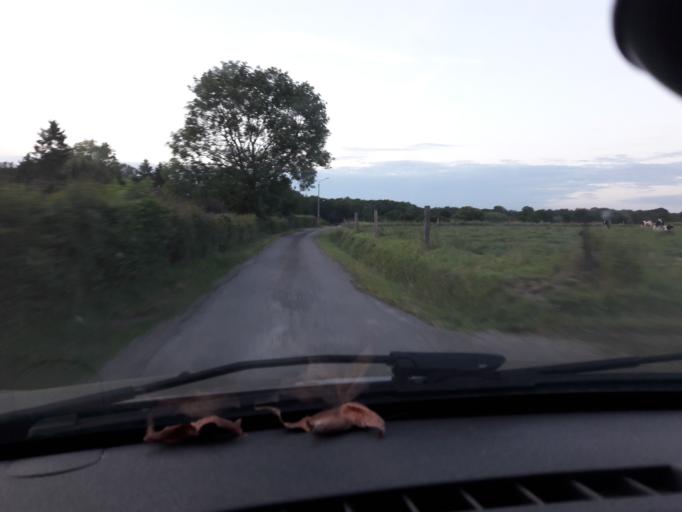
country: BE
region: Wallonia
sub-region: Province du Hainaut
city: Beaumont
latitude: 50.2656
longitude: 4.1878
